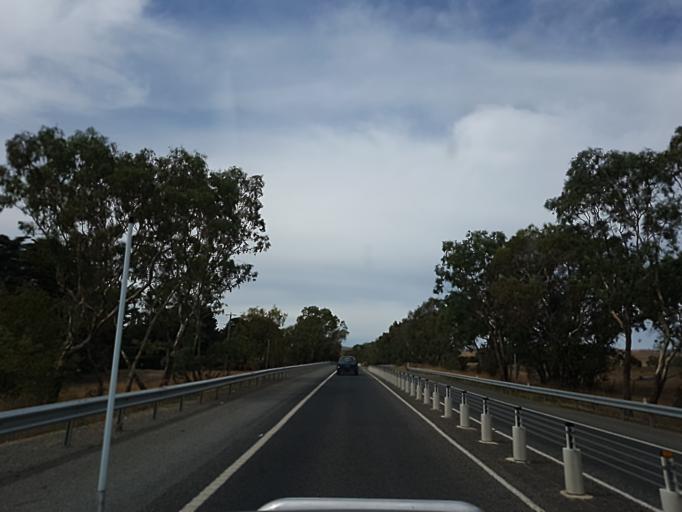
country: AU
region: Victoria
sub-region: Murrindindi
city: Alexandra
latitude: -37.2105
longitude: 145.4514
